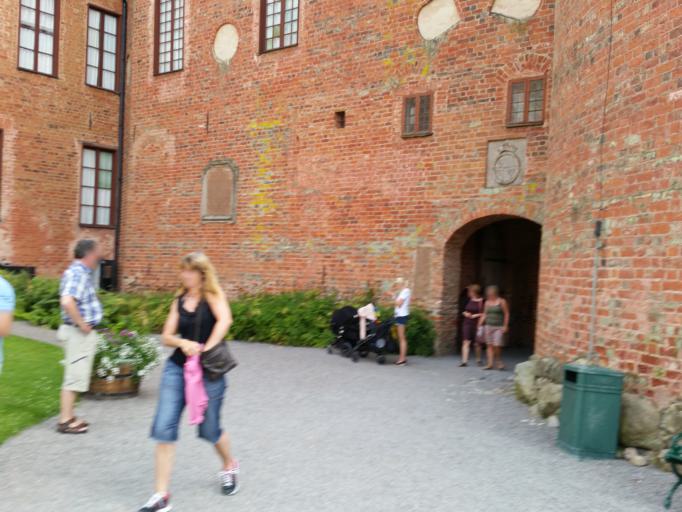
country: SE
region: Soedermanland
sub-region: Strangnas Kommun
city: Mariefred
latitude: 59.2561
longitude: 17.2195
